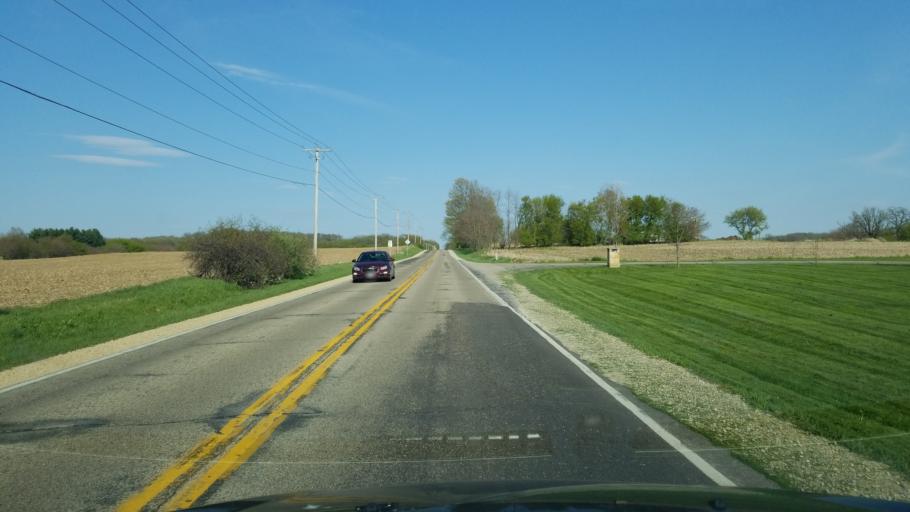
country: US
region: Wisconsin
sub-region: Dane County
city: Fitchburg
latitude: 42.9290
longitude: -89.4370
